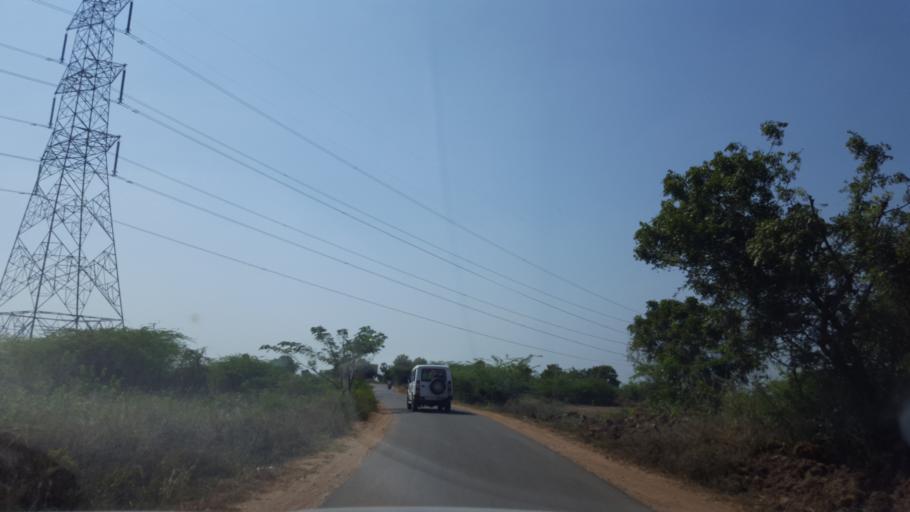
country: IN
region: Tamil Nadu
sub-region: Kancheepuram
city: Wallajahbad
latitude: 12.8597
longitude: 79.7919
